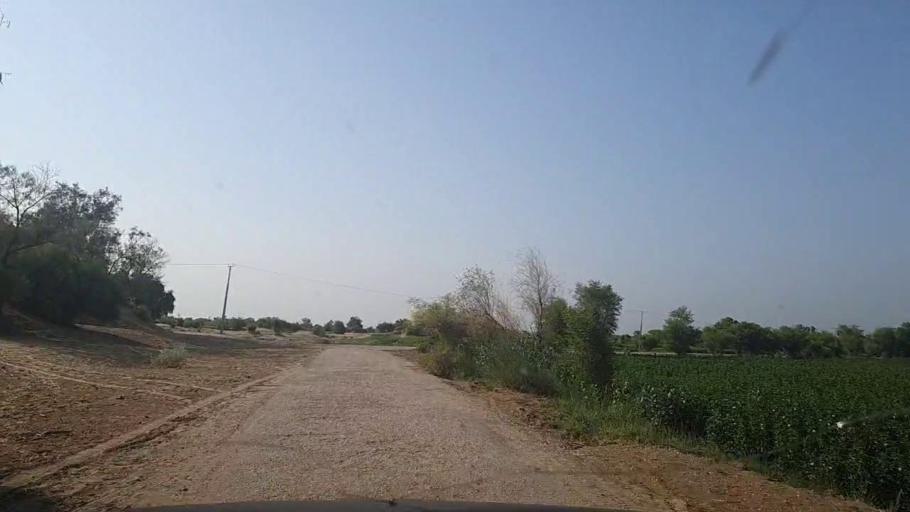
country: PK
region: Sindh
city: Khanpur
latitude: 27.7255
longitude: 69.3311
